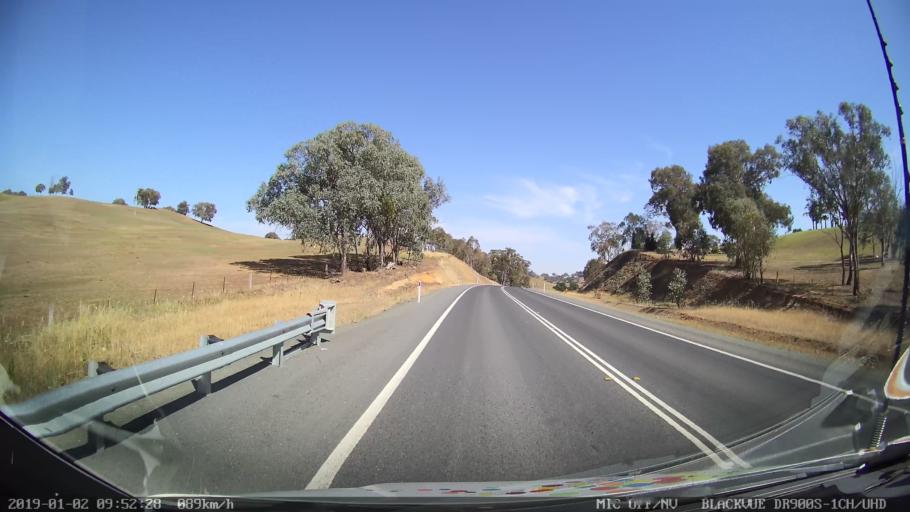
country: AU
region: New South Wales
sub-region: Tumut Shire
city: Tumut
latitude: -35.2605
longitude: 148.2059
